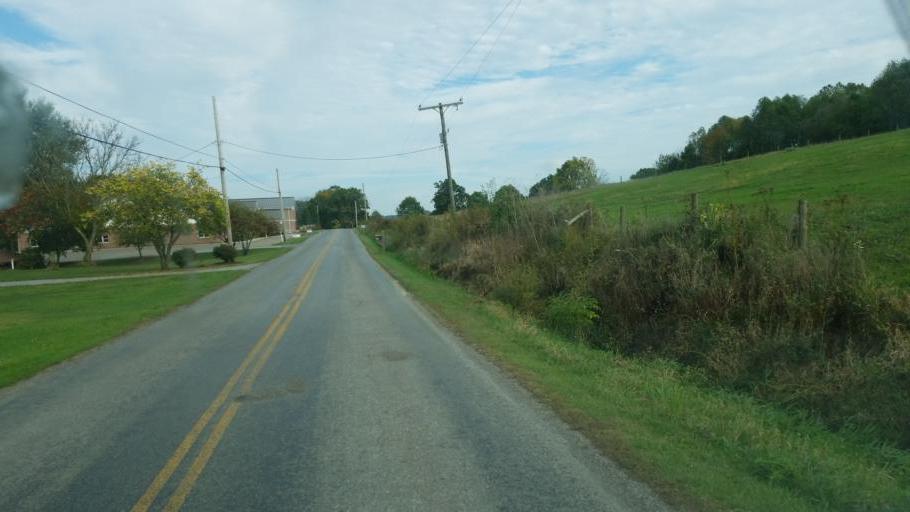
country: US
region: Ohio
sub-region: Holmes County
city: Millersburg
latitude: 40.5729
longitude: -81.8437
